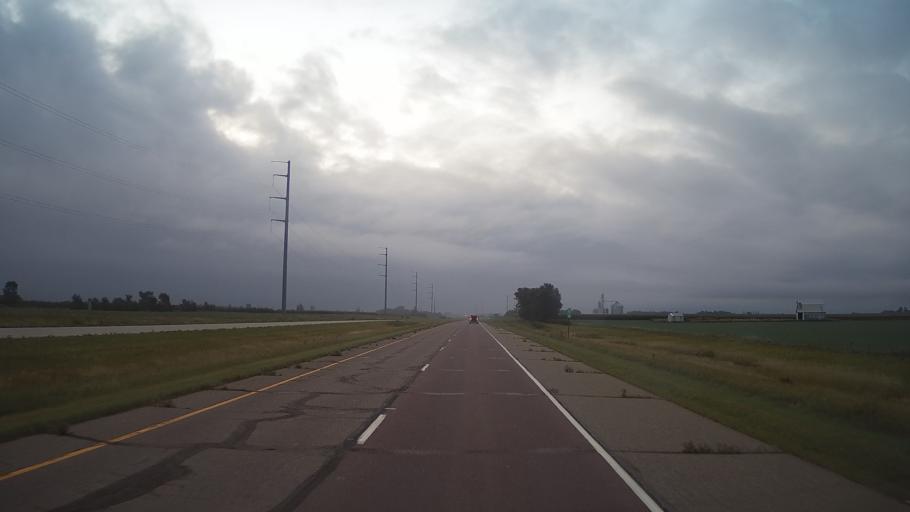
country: US
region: Minnesota
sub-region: Jackson County
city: Lakefield
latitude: 43.6374
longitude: -95.3505
